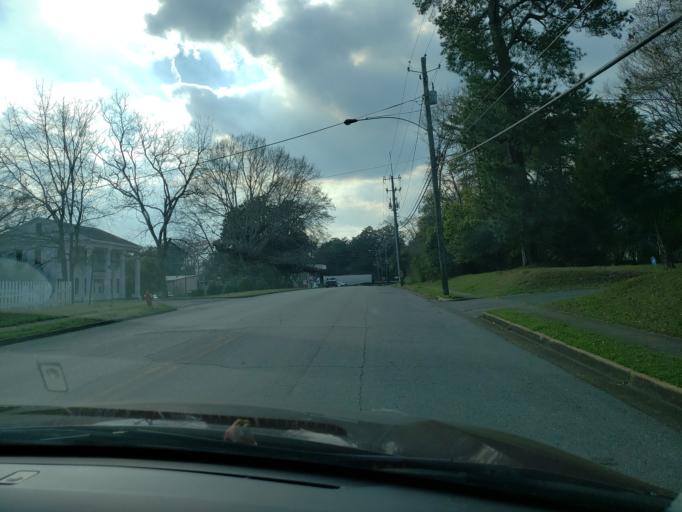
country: US
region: Alabama
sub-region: Hale County
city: Greensboro
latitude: 32.7042
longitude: -87.6050
